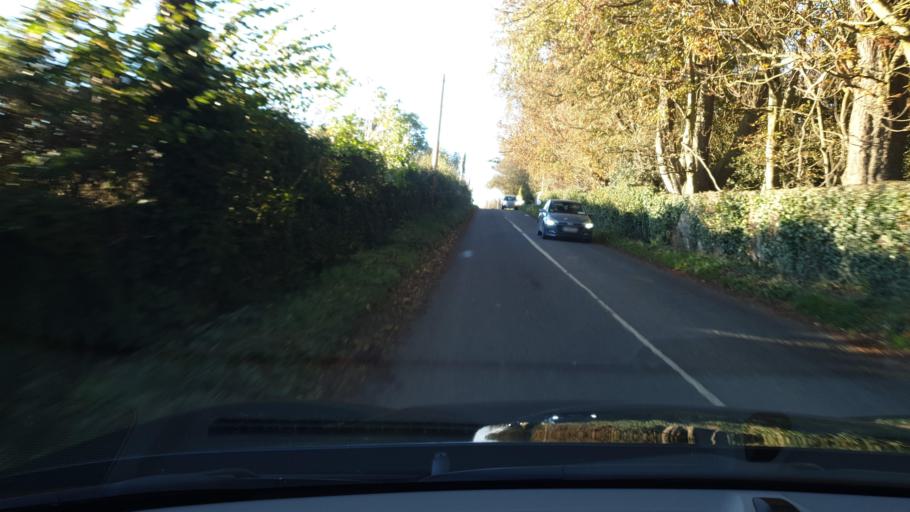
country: IE
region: Leinster
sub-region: Lu
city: Drogheda
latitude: 53.6700
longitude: -6.3194
